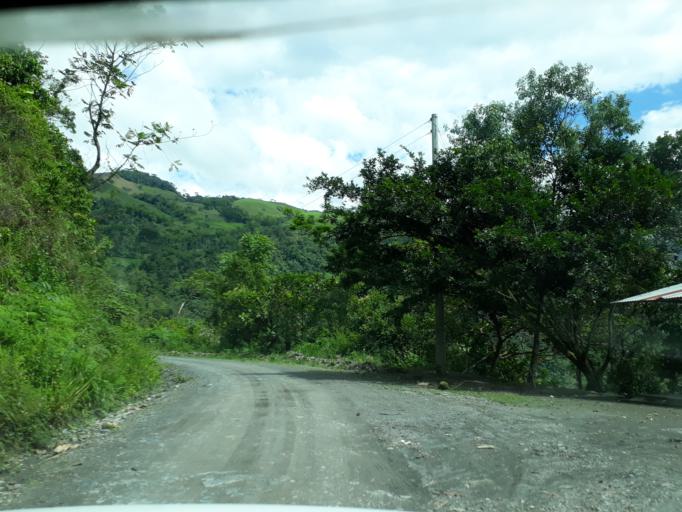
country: CO
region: Boyaca
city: Quipama
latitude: 5.4439
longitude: -74.1808
